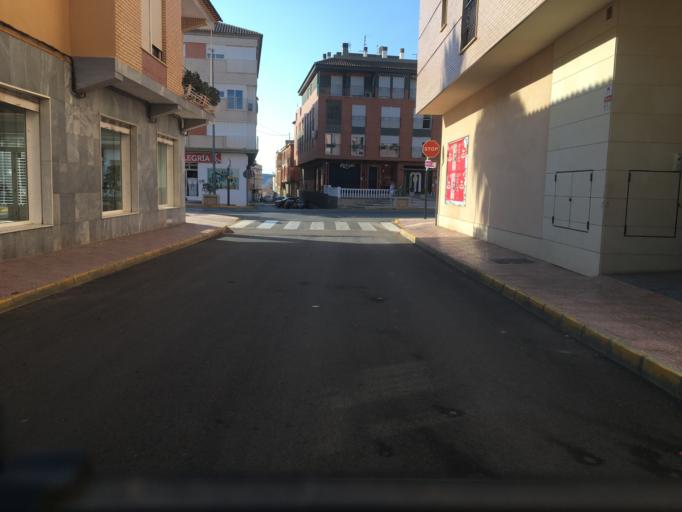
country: ES
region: Murcia
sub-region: Murcia
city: Puerto Lumbreras
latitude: 37.5659
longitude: -1.8054
